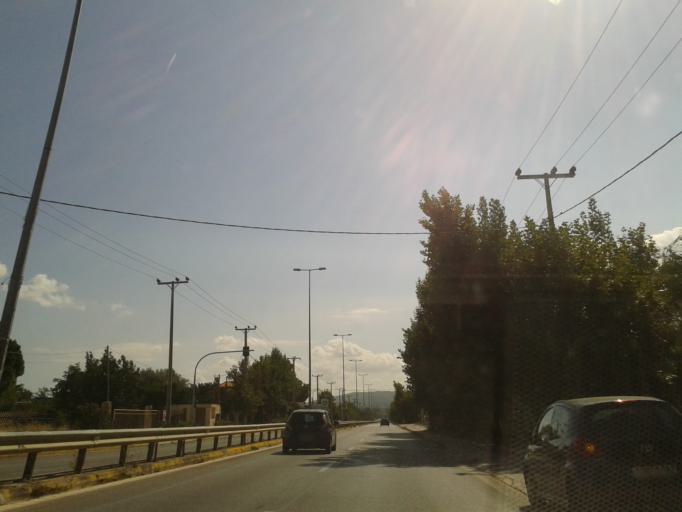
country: GR
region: Attica
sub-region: Nomarchia Anatolikis Attikis
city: Aghios Panteleimon
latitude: 38.1151
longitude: 23.9697
